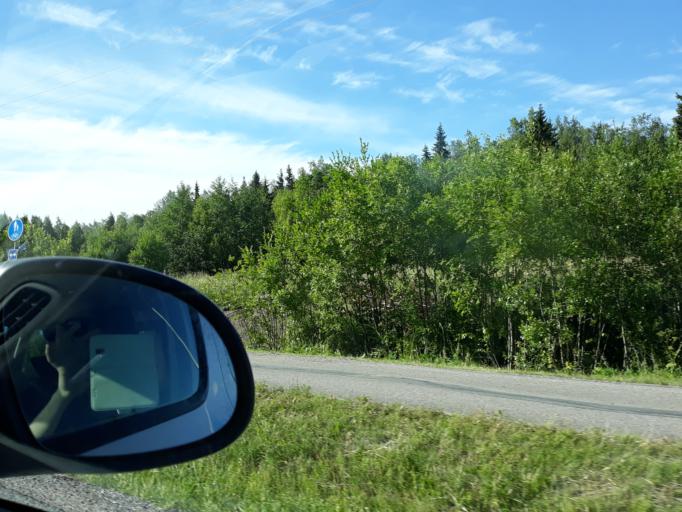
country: FI
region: Uusimaa
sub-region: Helsinki
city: Jaervenpaeae
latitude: 60.5427
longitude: 24.9880
